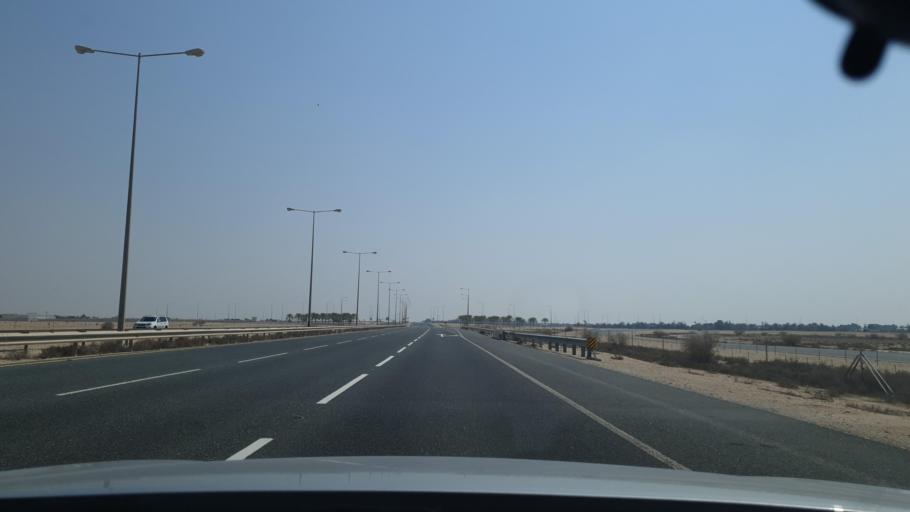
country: QA
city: Al Ghuwayriyah
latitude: 25.7909
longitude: 51.3913
